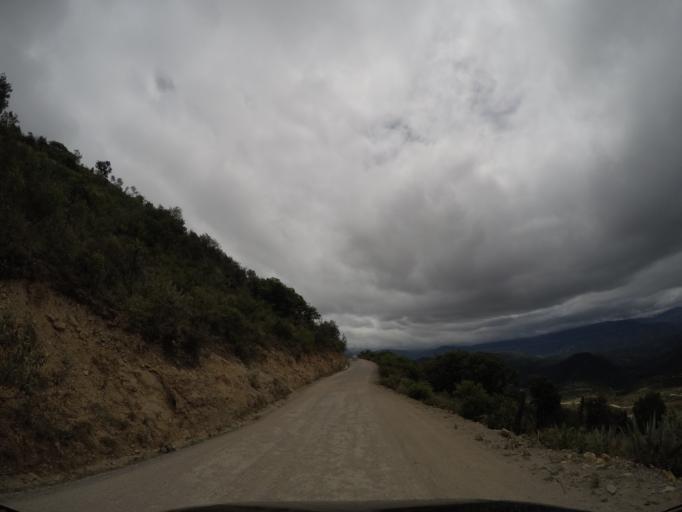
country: MX
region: Oaxaca
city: San Lorenzo Albarradas
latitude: 16.8921
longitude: -96.2635
